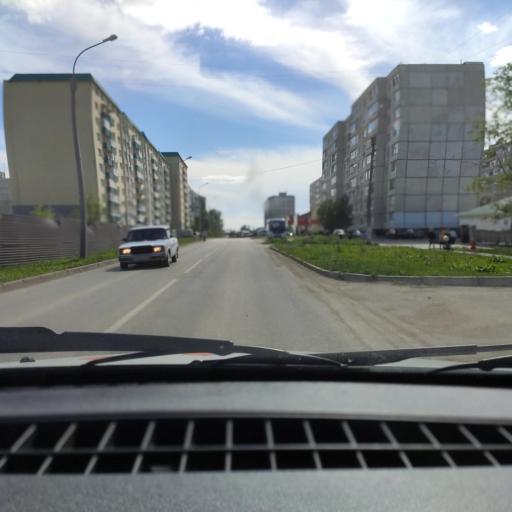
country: RU
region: Bashkortostan
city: Blagoveshchensk
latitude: 55.0519
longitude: 55.9619
